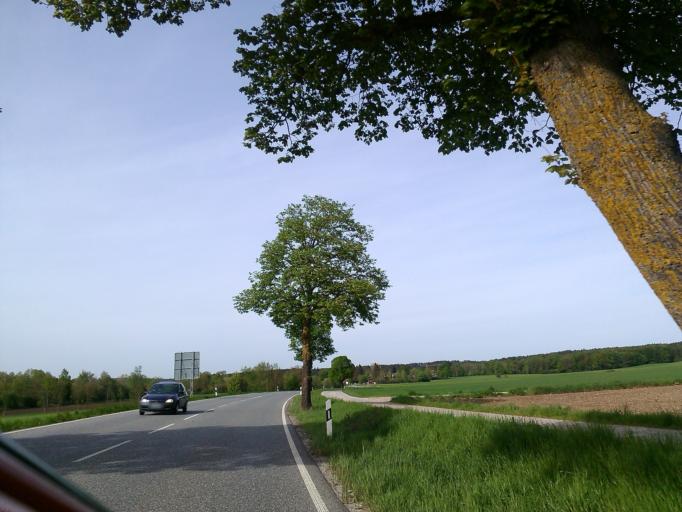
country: DE
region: Bavaria
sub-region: Upper Bavaria
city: Feldafing
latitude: 47.9479
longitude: 11.2623
